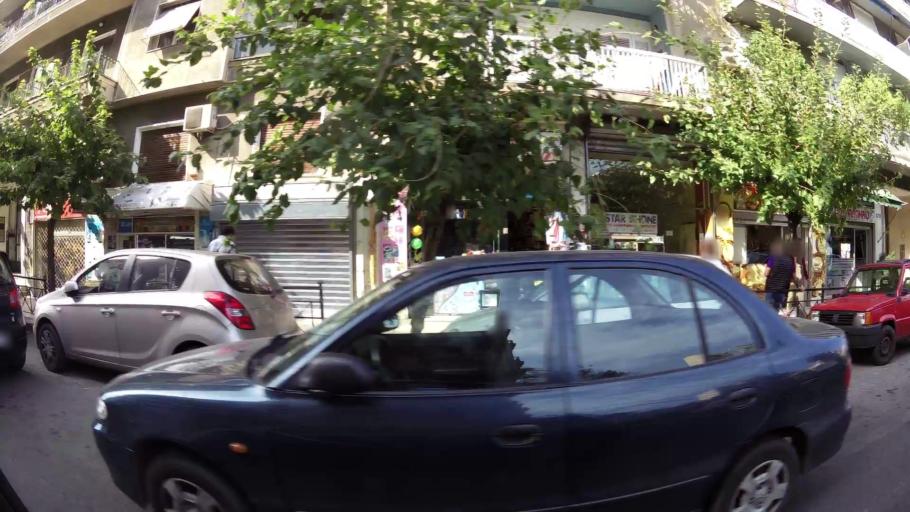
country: GR
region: Attica
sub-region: Nomarchia Athinas
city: Kipseli
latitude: 37.9930
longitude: 23.7289
